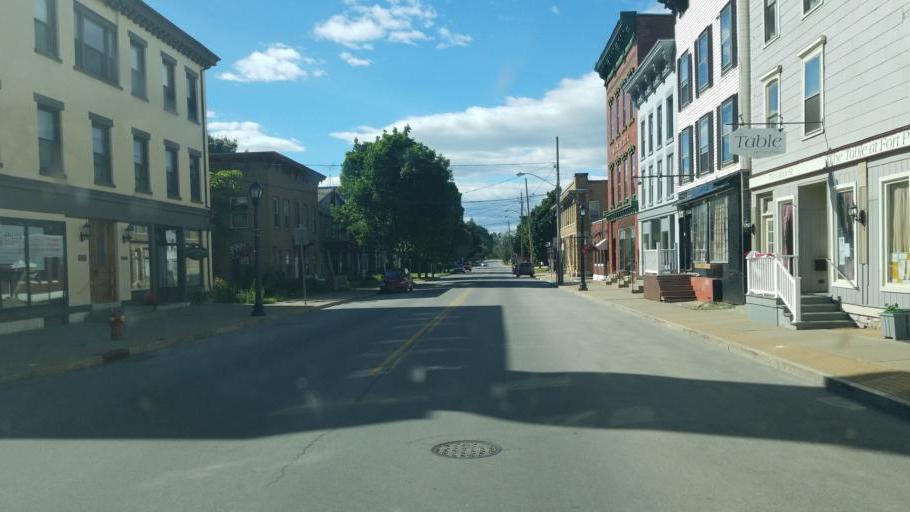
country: US
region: New York
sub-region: Montgomery County
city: Fort Plain
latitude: 42.9319
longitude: -74.6235
